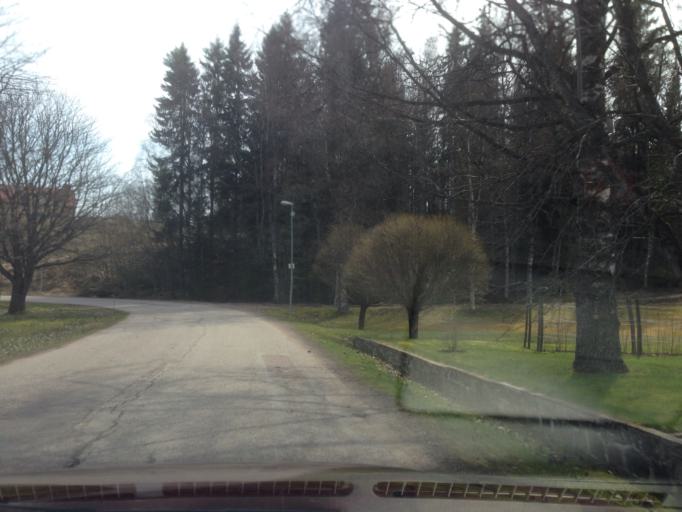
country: SE
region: Dalarna
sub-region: Ludvika Kommun
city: Grangesberg
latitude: 60.1450
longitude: 14.9842
